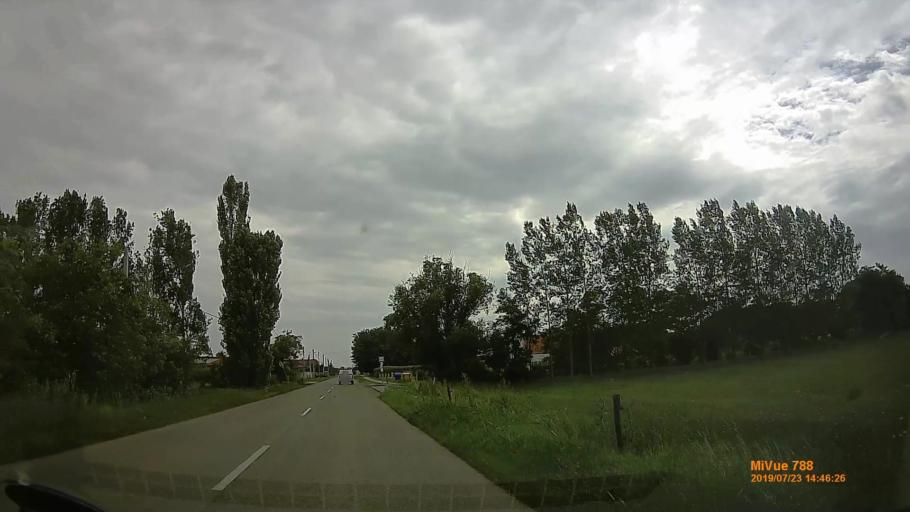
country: HU
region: Szabolcs-Szatmar-Bereg
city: Nyiregyhaza
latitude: 47.9189
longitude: 21.6764
